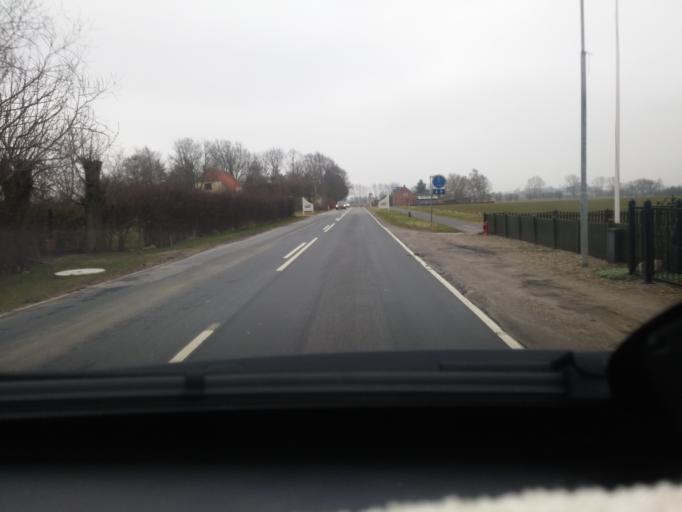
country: DK
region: South Denmark
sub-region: Nyborg Kommune
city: Ullerslev
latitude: 55.3813
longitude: 10.7250
